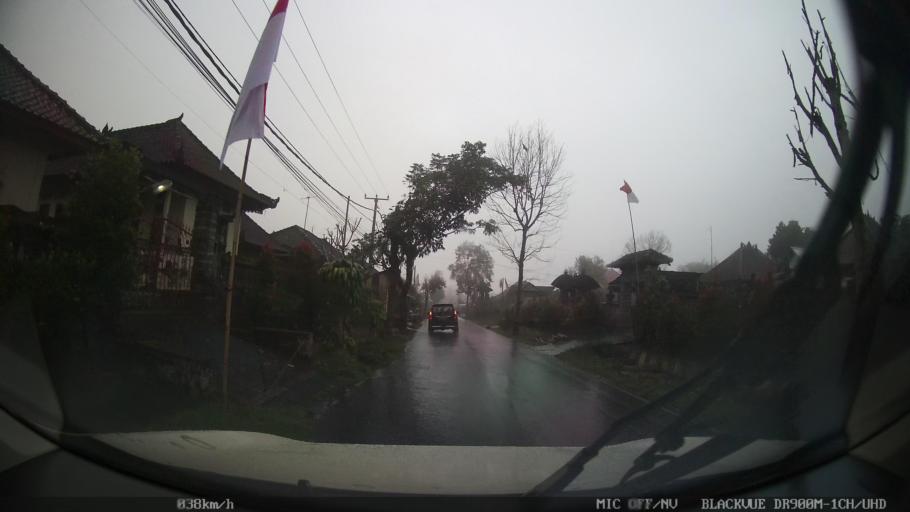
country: ID
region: Bali
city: Banjar Taro Kelod
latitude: -8.3229
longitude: 115.2951
